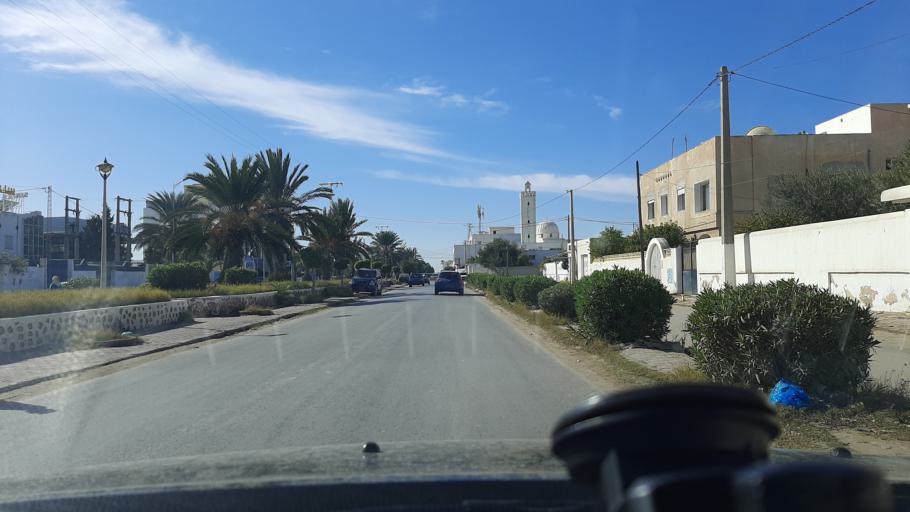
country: TN
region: Safaqis
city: Sfax
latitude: 34.7226
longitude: 10.7352
